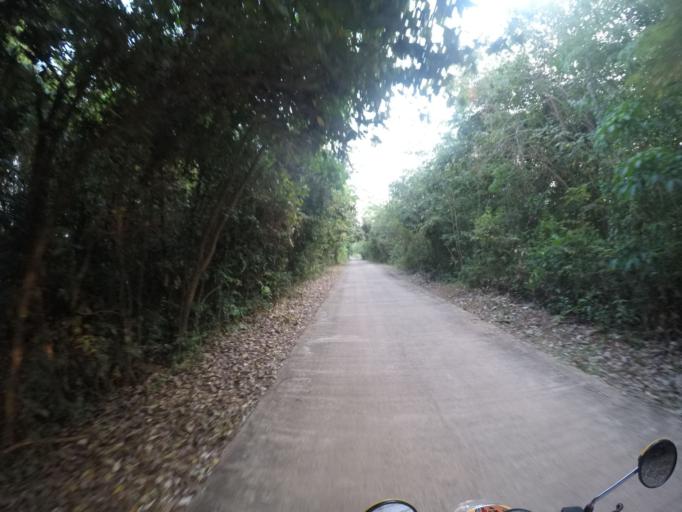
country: TH
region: Trat
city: Ko Kut
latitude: 11.8005
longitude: 102.4862
